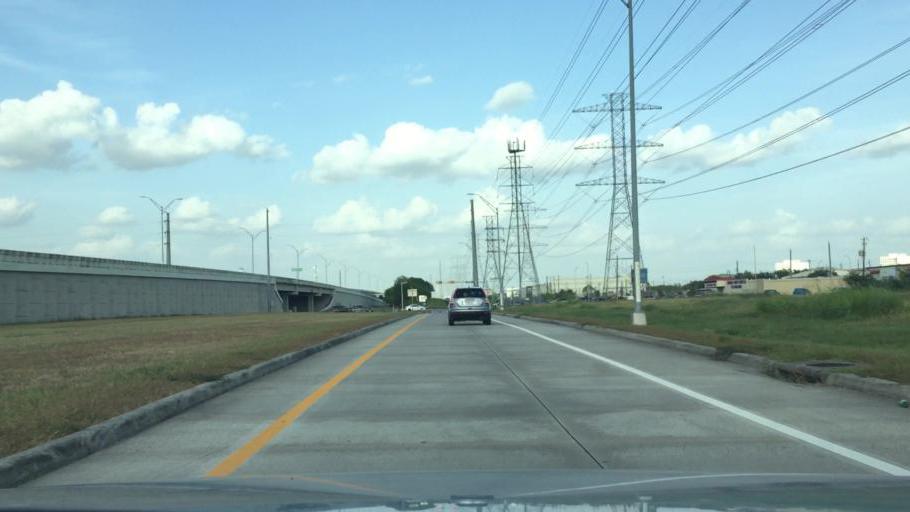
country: US
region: Texas
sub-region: Harris County
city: Piney Point Village
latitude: 29.7217
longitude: -95.5221
